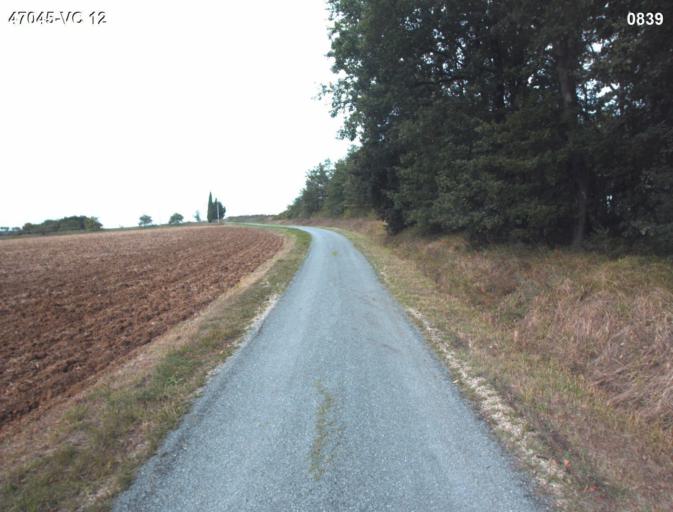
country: FR
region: Aquitaine
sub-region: Departement du Lot-et-Garonne
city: Nerac
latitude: 44.1437
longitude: 0.4259
